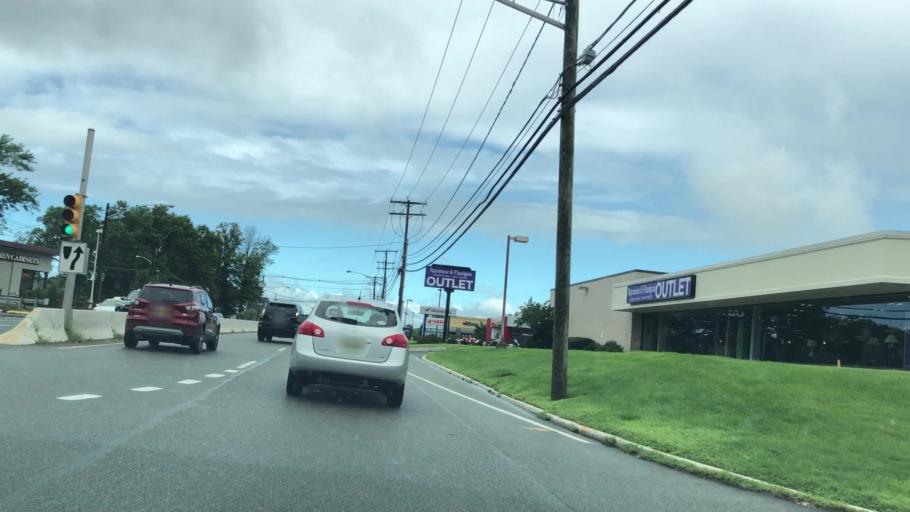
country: US
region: New Jersey
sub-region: Morris County
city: Hanover
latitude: 40.8075
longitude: -74.3745
